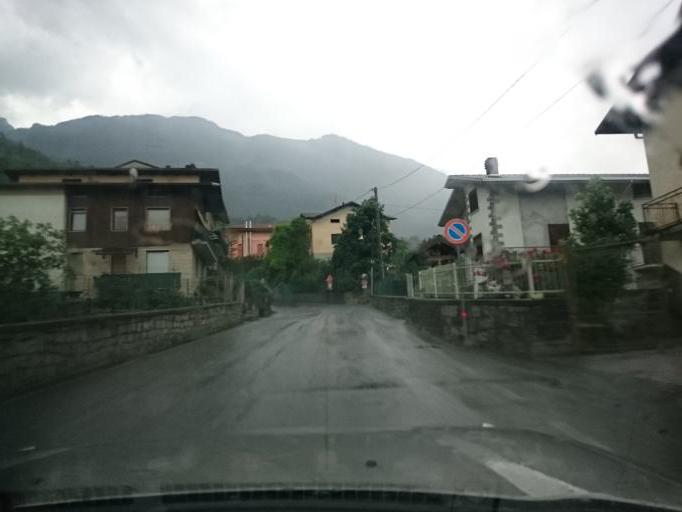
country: IT
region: Lombardy
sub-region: Provincia di Brescia
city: Ceto
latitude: 46.0110
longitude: 10.3510
